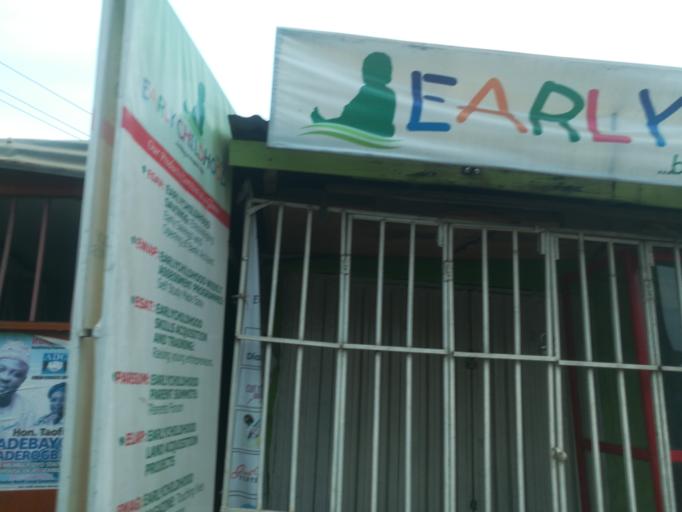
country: NG
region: Oyo
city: Ibadan
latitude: 7.4421
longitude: 3.9109
